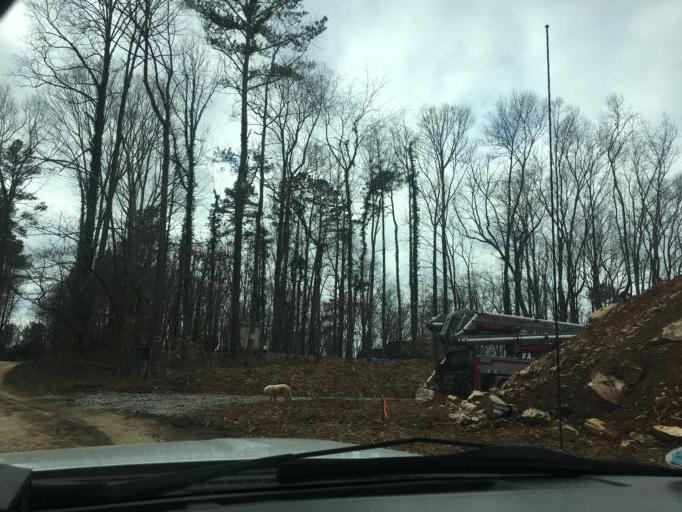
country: US
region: Georgia
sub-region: Fulton County
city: Milton
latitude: 34.2080
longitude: -84.3140
